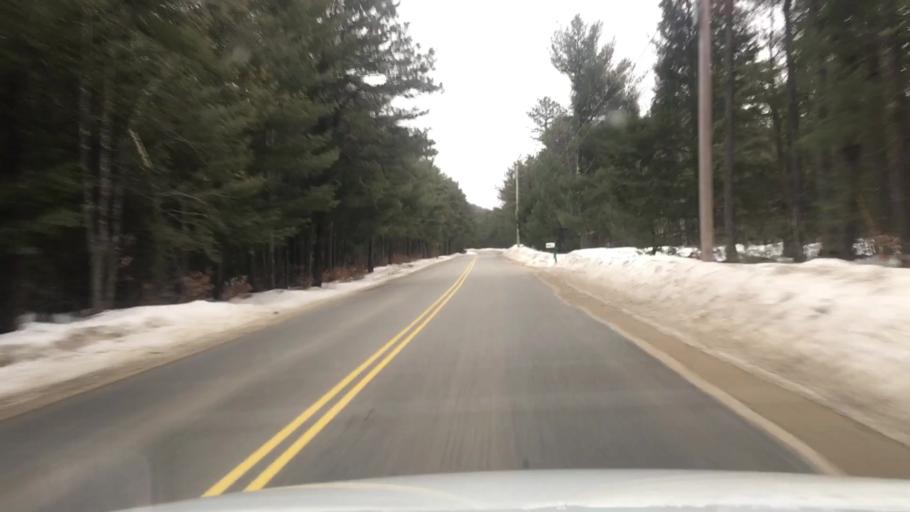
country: US
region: Maine
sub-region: York County
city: Newfield
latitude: 43.6019
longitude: -70.8806
